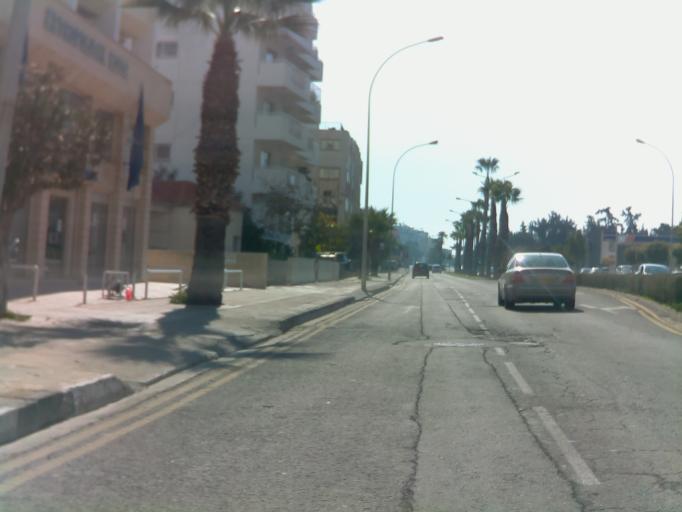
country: CY
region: Larnaka
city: Larnaca
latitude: 34.9085
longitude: 33.6296
